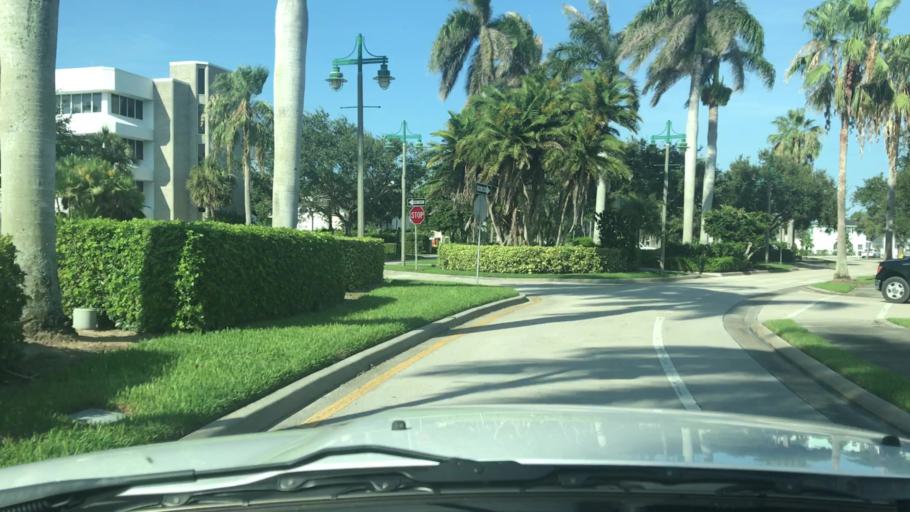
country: US
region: Florida
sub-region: Indian River County
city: Vero Beach
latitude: 27.6467
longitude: -80.3809
